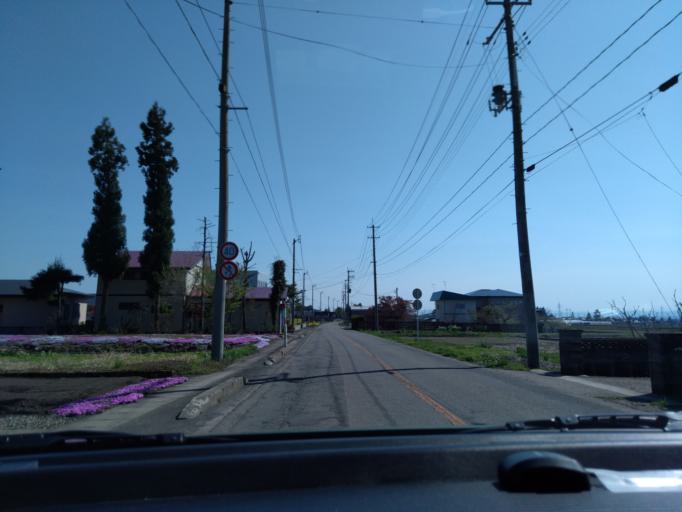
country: JP
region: Akita
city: Omagari
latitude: 39.4716
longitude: 140.5846
